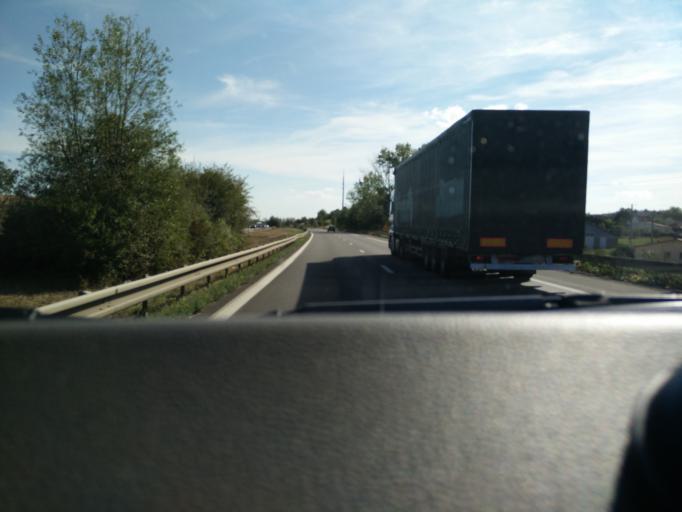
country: FR
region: Lorraine
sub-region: Departement de la Moselle
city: Corny-sur-Moselle
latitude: 49.0005
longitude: 6.1058
